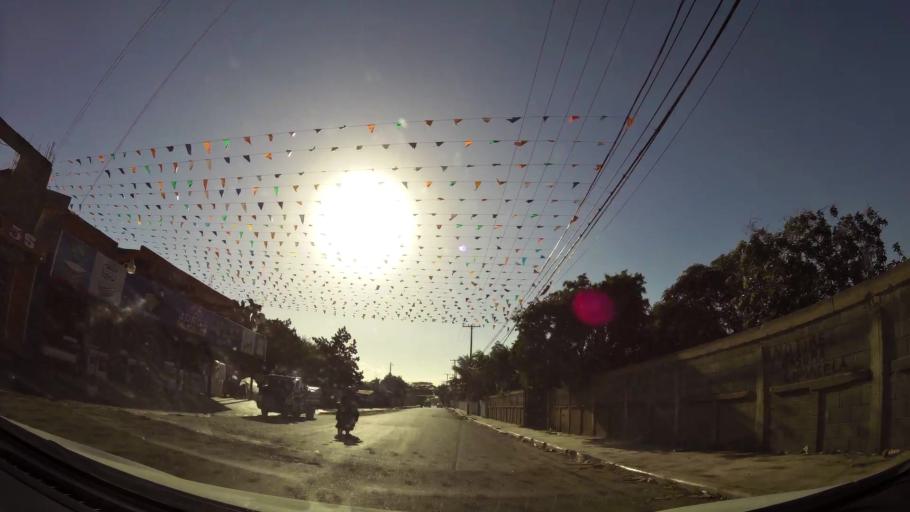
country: DO
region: Santo Domingo
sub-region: Santo Domingo
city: Santo Domingo Este
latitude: 18.4809
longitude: -69.8194
